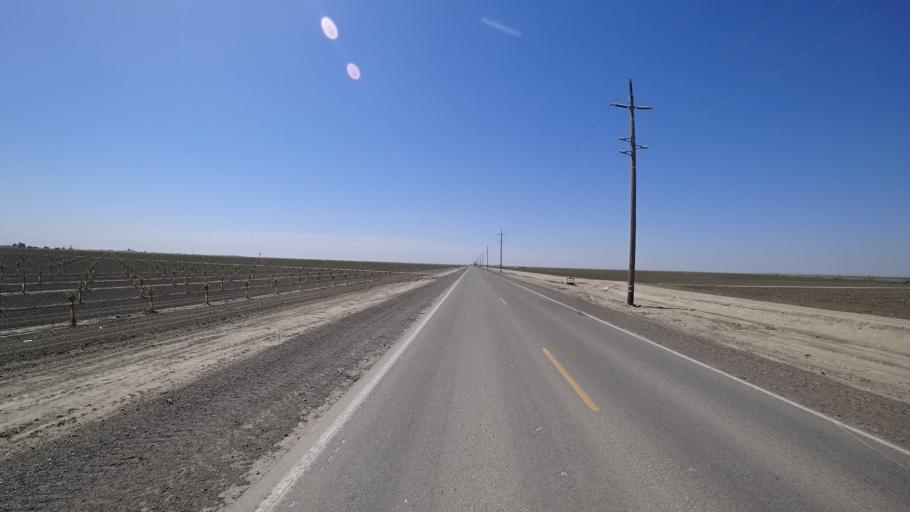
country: US
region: California
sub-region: Kings County
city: Corcoran
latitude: 36.0584
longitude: -119.5720
